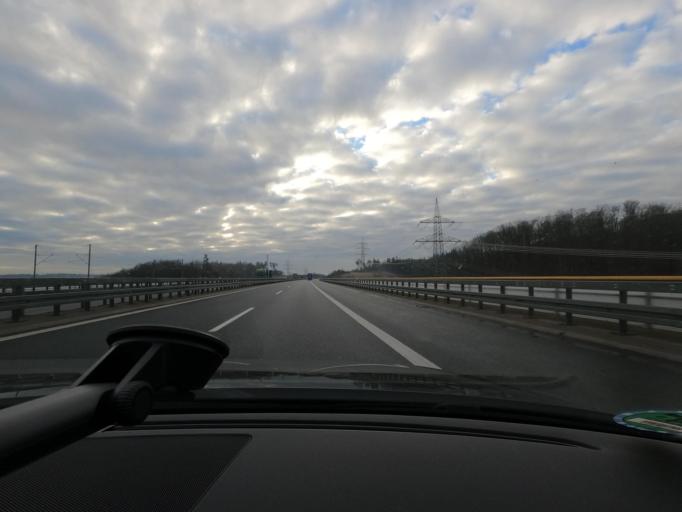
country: DE
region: Bavaria
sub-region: Upper Franconia
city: Rodental
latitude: 50.2807
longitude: 11.0151
